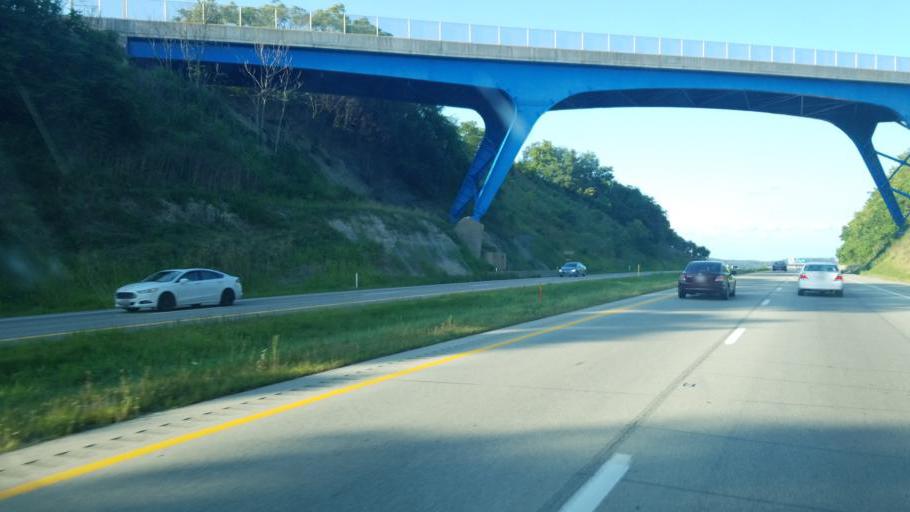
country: US
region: Pennsylvania
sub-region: Washington County
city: Canonsburg
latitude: 40.2486
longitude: -80.1942
